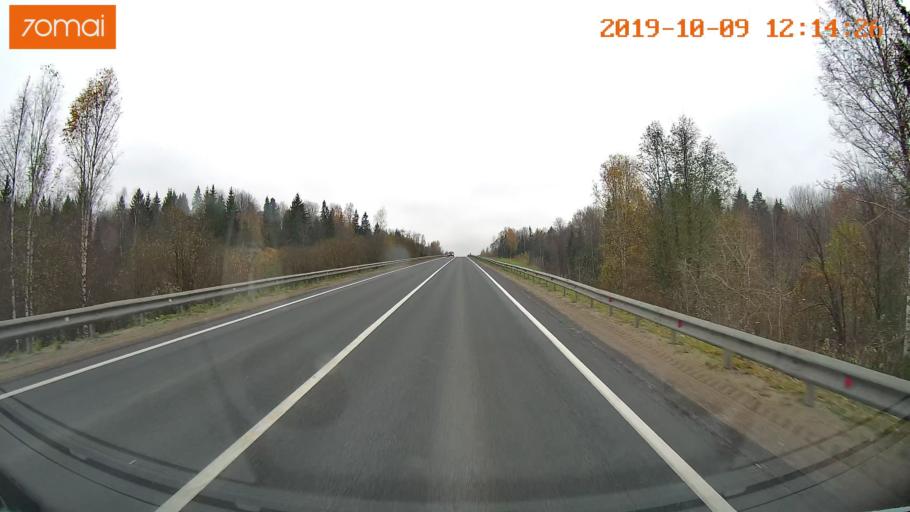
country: RU
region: Jaroslavl
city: Prechistoye
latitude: 58.4963
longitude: 40.3368
